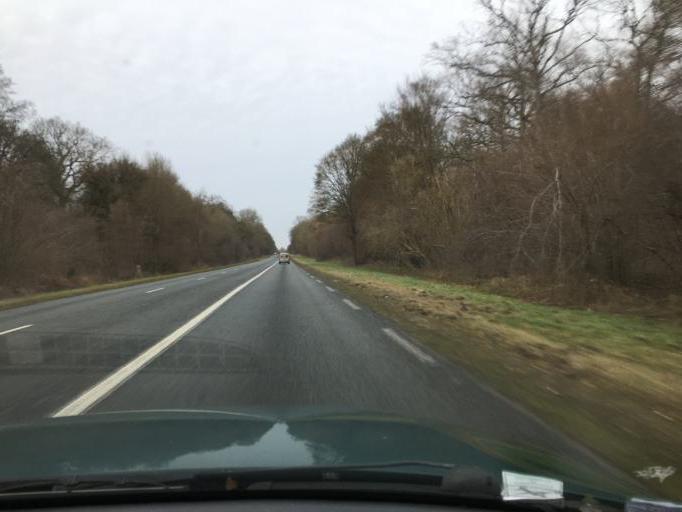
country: FR
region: Picardie
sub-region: Departement de l'Oise
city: Senlis
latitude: 49.1815
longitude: 2.5673
